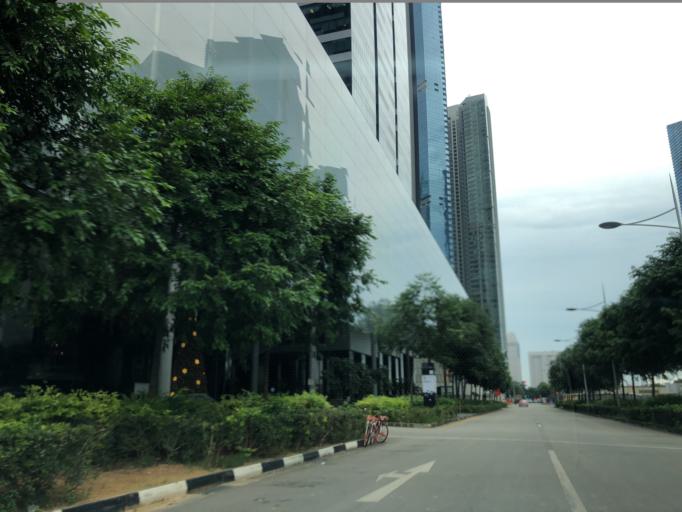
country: SG
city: Singapore
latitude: 1.2779
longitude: 103.8511
